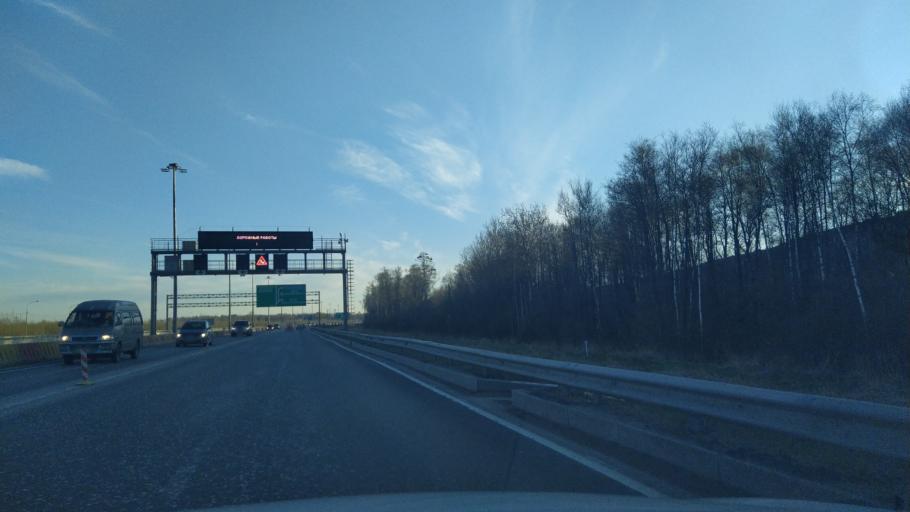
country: RU
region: St.-Petersburg
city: Levashovo
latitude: 60.0710
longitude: 30.1750
